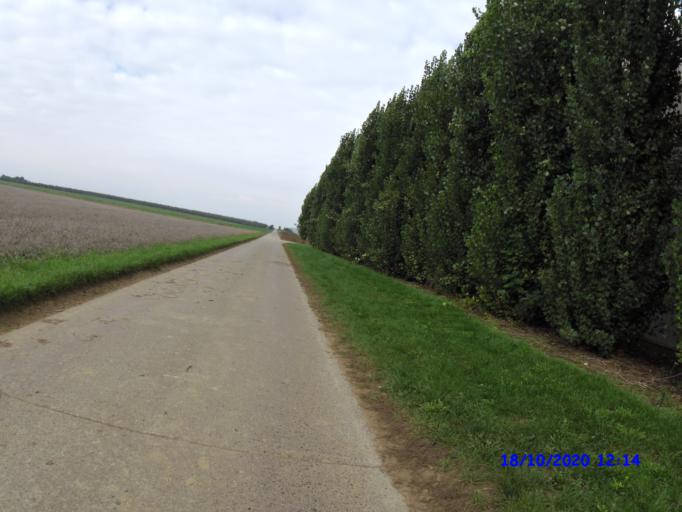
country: BE
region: Flanders
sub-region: Provincie Vlaams-Brabant
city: Landen
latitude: 50.7663
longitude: 5.0615
